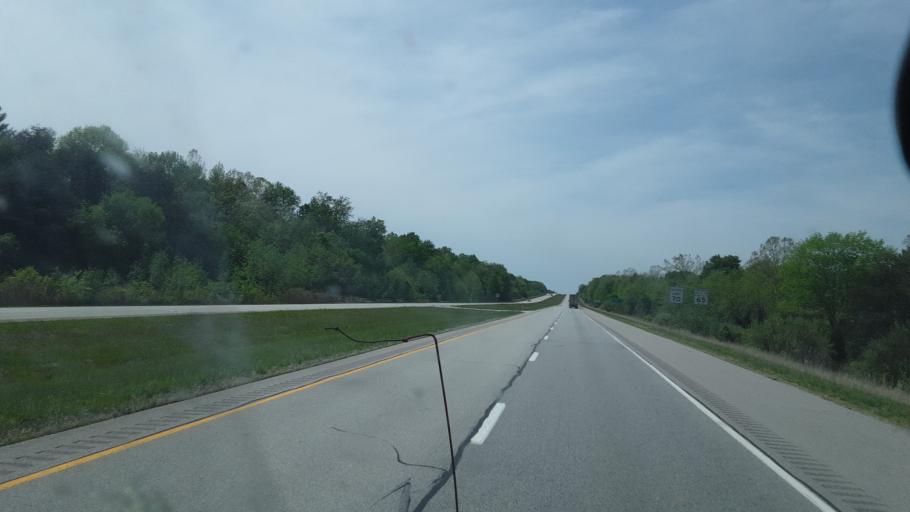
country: US
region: Indiana
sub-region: Warrick County
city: Boonville
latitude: 38.1925
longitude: -87.3045
